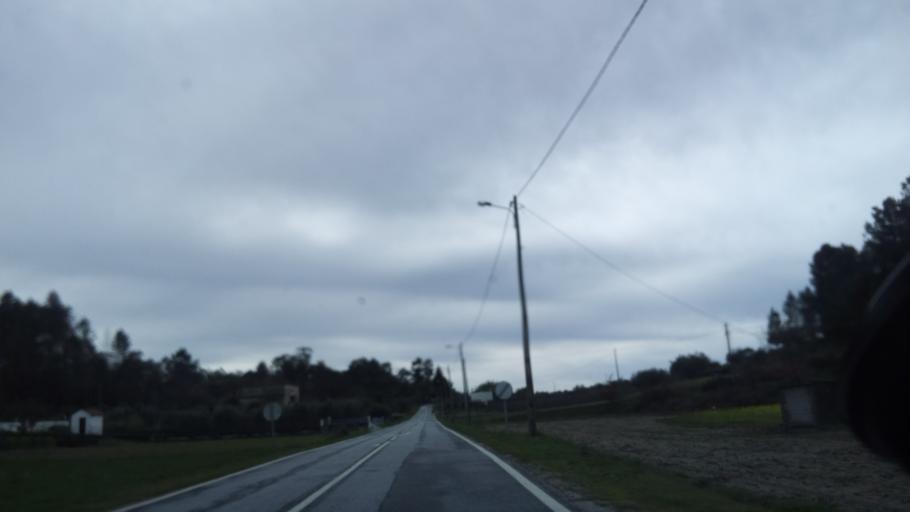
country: PT
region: Guarda
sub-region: Seia
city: Seia
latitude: 40.4845
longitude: -7.6631
